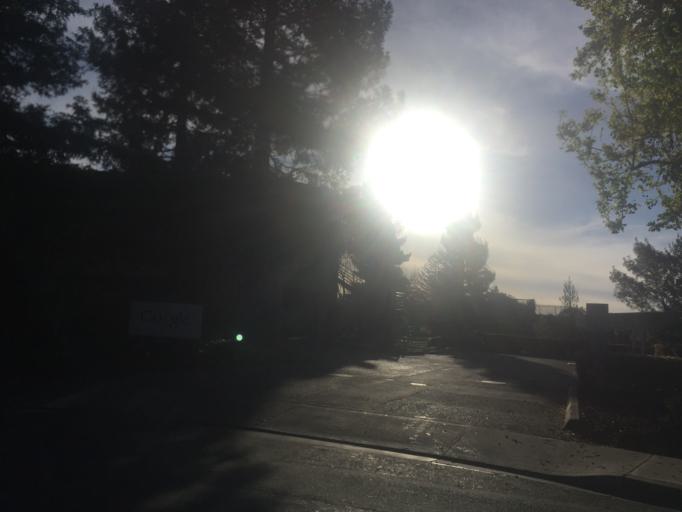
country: US
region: California
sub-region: Santa Clara County
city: Mountain View
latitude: 37.4213
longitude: -122.0909
